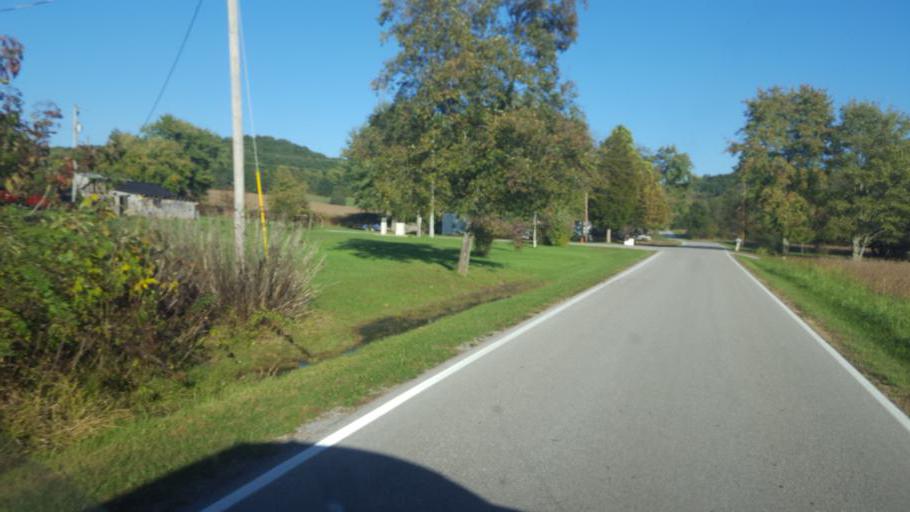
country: US
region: Ohio
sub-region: Adams County
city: Manchester
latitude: 38.5094
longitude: -83.5335
